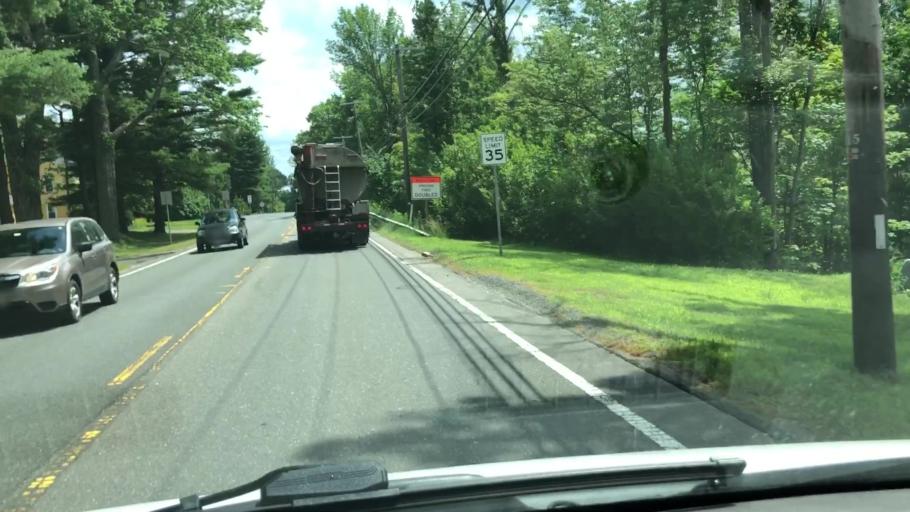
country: US
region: Massachusetts
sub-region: Hampshire County
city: Chesterfield
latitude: 42.4368
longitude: -72.7982
